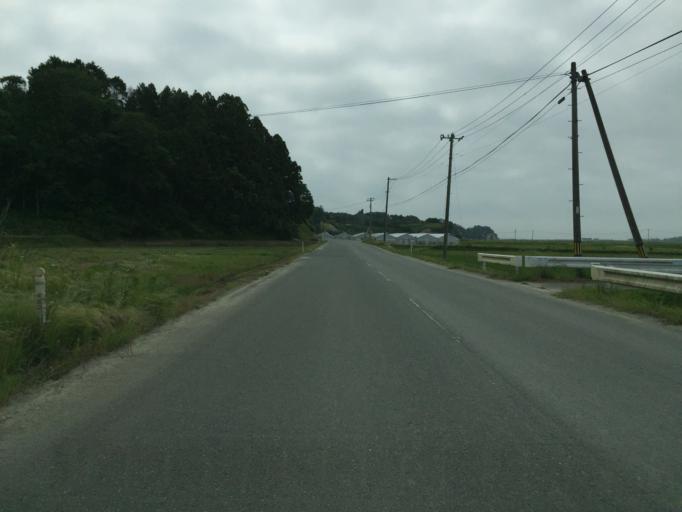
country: JP
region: Fukushima
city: Namie
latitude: 37.7398
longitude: 140.9887
